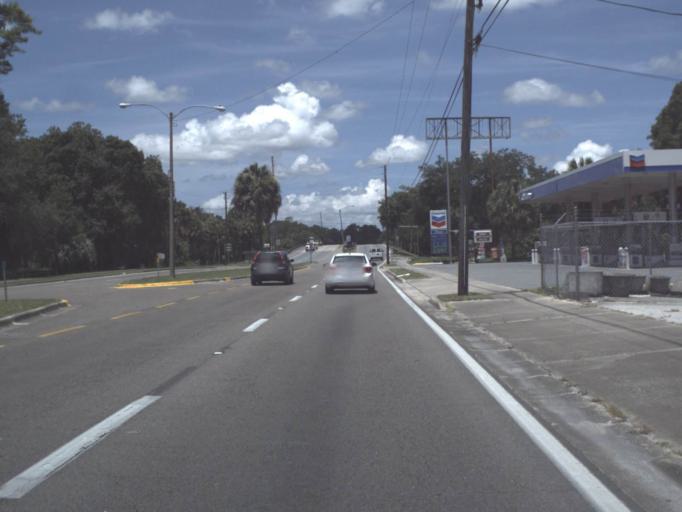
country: US
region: Florida
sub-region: Levy County
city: Manatee Road
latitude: 29.5912
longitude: -82.9340
